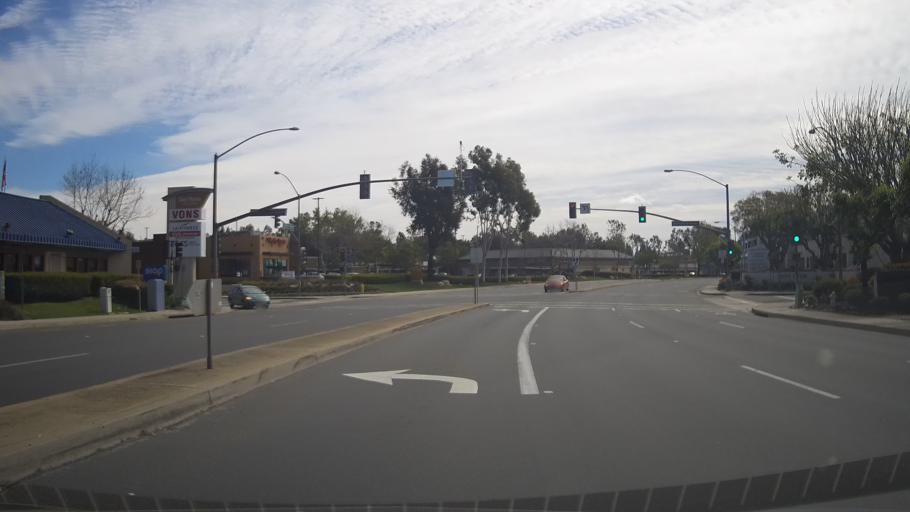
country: US
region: California
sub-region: San Diego County
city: Escondido
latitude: 33.1436
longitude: -117.0967
